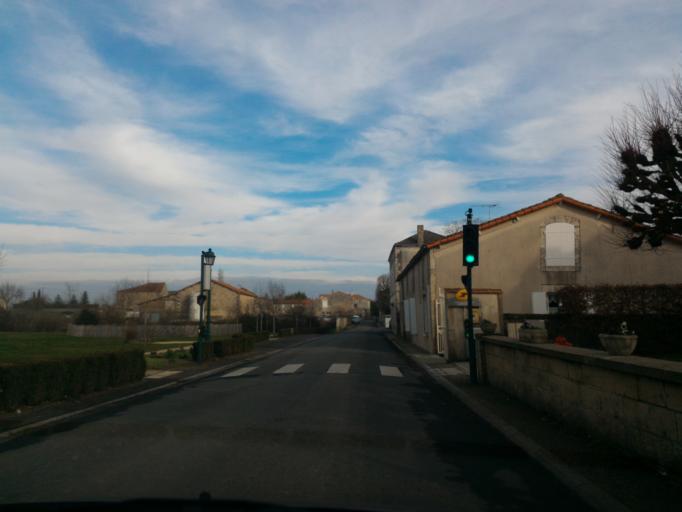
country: FR
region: Poitou-Charentes
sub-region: Departement de la Charente
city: Villefagnan
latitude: 45.9871
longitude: 0.1335
